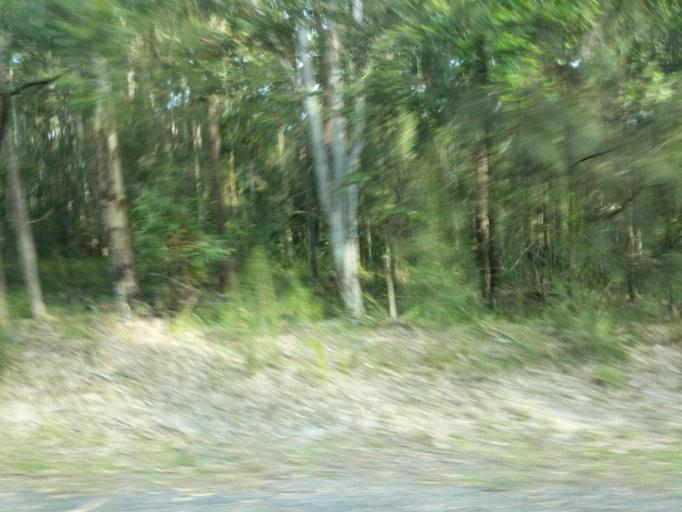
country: AU
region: New South Wales
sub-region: Port Stephens Shire
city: Port Stephens
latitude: -32.6644
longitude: 152.0191
